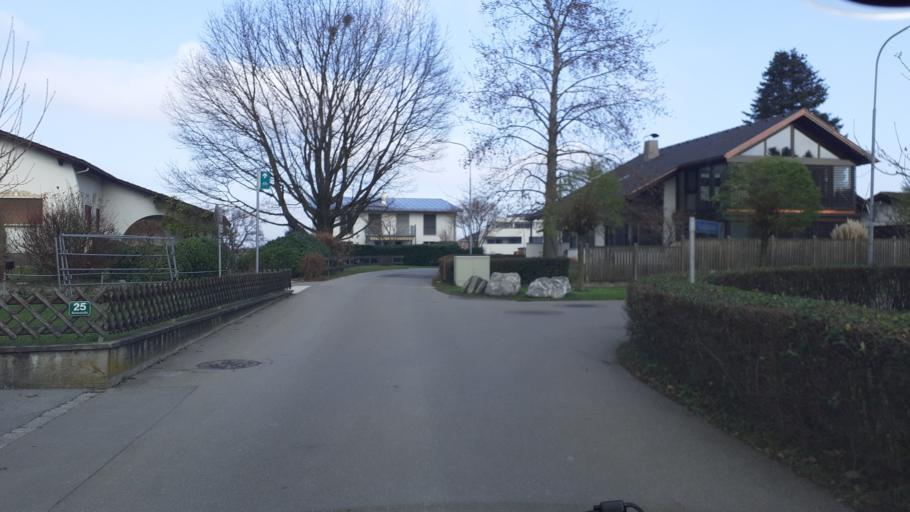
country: AT
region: Vorarlberg
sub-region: Politischer Bezirk Bregenz
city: Hochst
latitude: 47.4653
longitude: 9.6470
